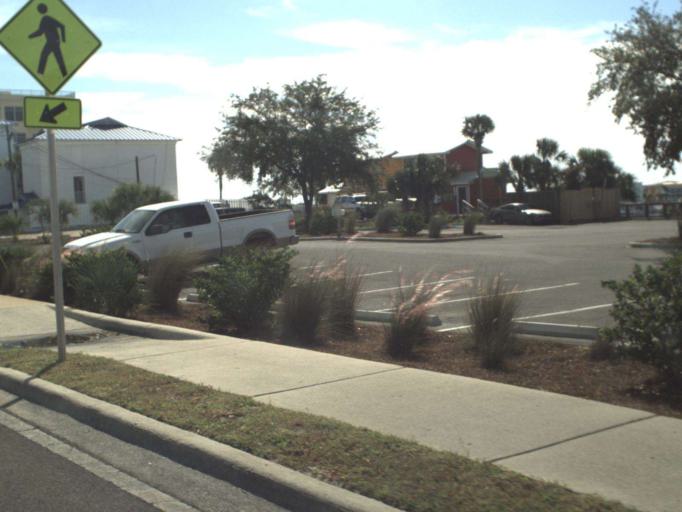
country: US
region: Florida
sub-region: Okaloosa County
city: Destin
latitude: 30.3930
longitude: -86.5000
